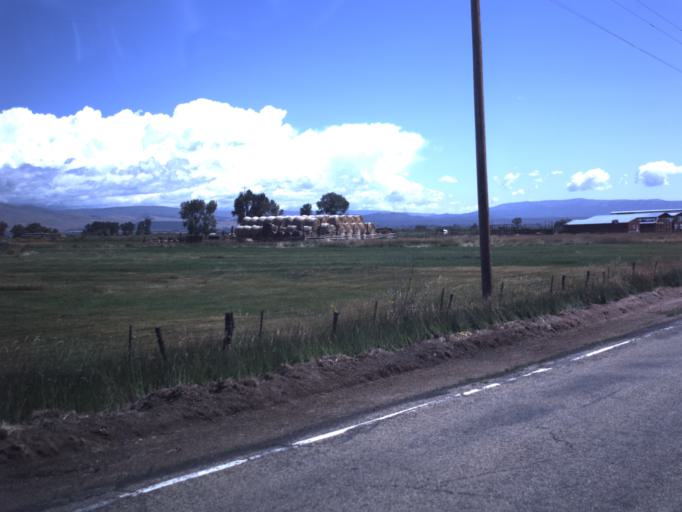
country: US
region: Utah
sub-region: Duchesne County
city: Roosevelt
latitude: 40.4329
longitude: -109.9852
